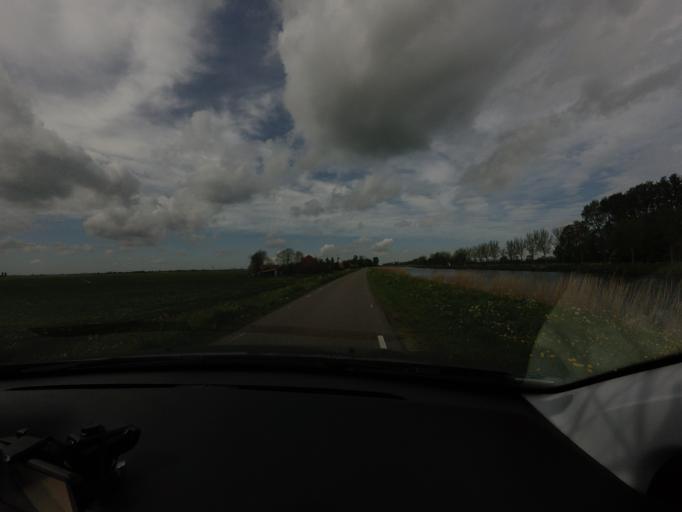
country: NL
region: North Holland
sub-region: Gemeente Beemster
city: Halfweg
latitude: 52.5174
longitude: 4.8934
